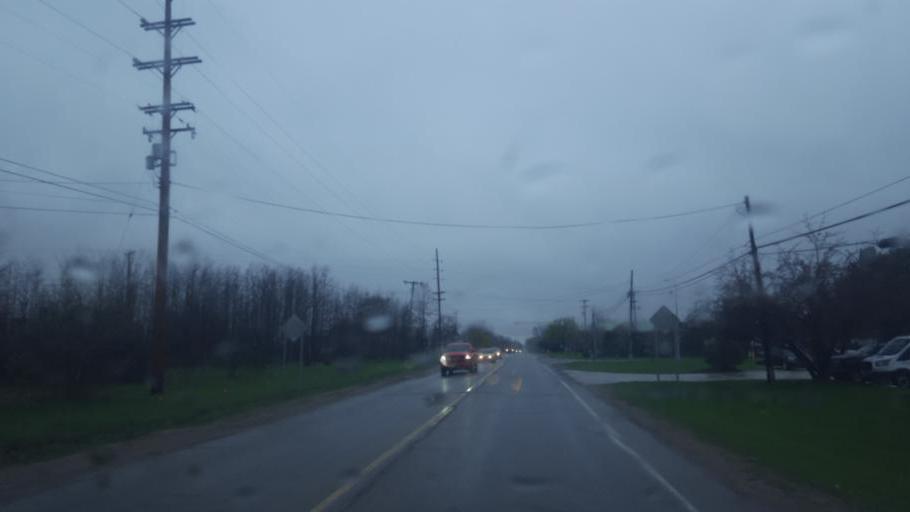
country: US
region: Michigan
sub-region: Isabella County
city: Mount Pleasant
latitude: 43.6184
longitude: -84.7679
